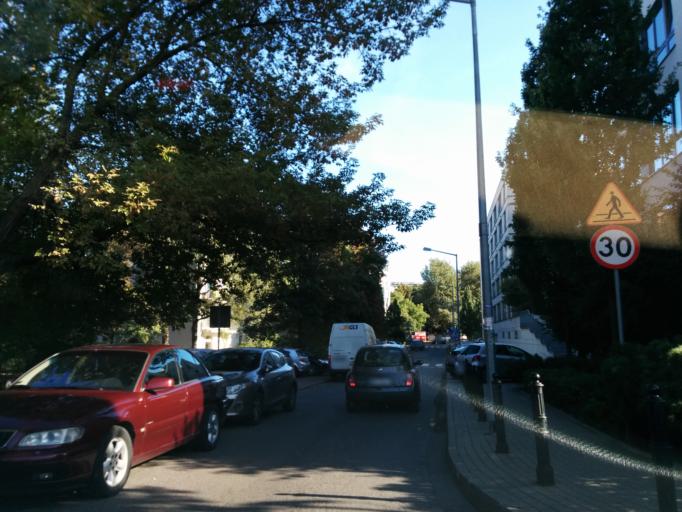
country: PL
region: Masovian Voivodeship
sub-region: Warszawa
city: Zoliborz
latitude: 52.2712
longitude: 20.9827
